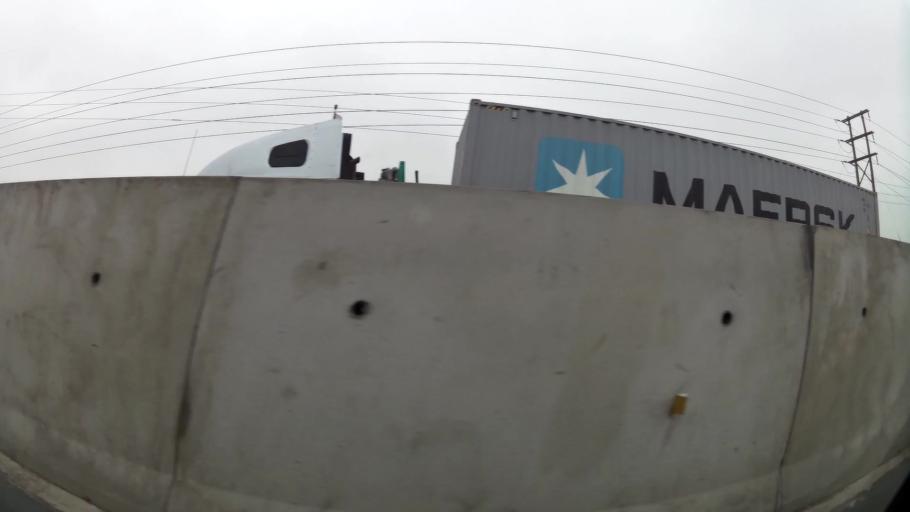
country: PE
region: Lima
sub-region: Lima
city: Urb. Santo Domingo
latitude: -11.9290
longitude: -77.0726
